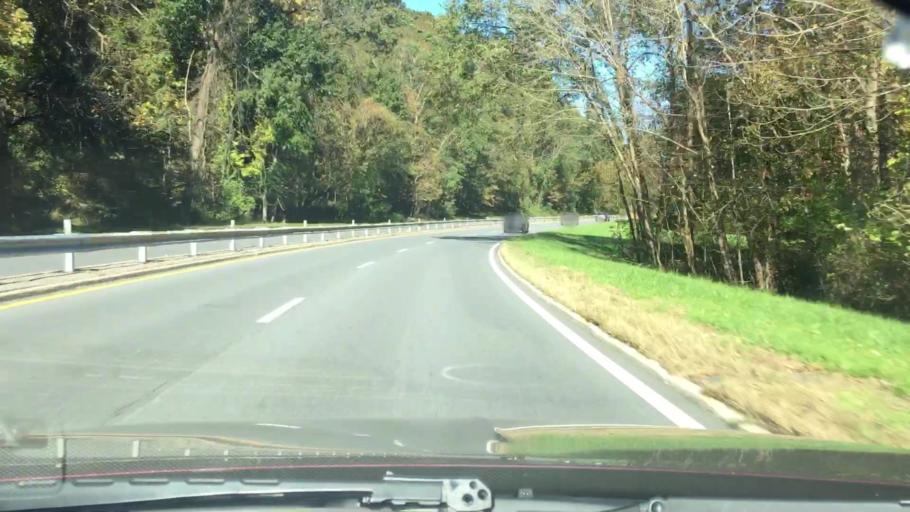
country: US
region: New York
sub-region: Westchester County
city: Mount Kisco
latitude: 41.1981
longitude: -73.7443
